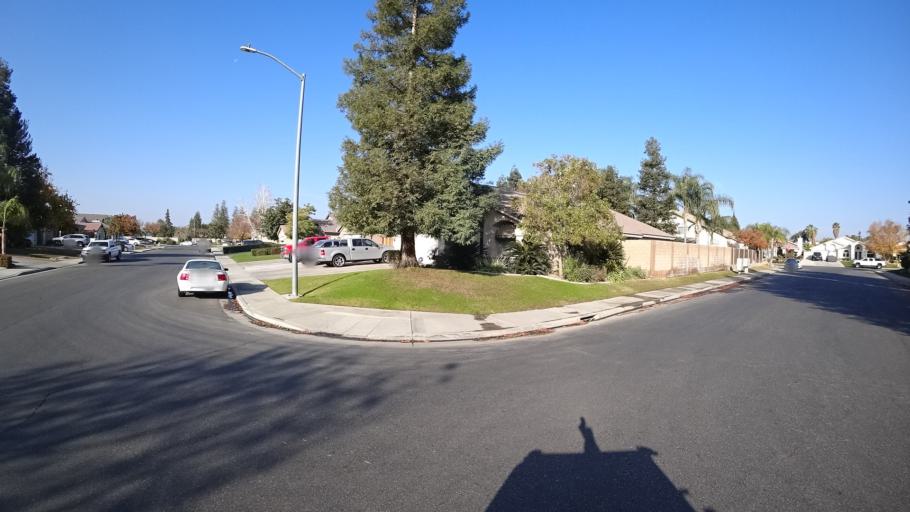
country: US
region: California
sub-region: Kern County
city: Greenacres
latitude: 35.3666
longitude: -119.1173
